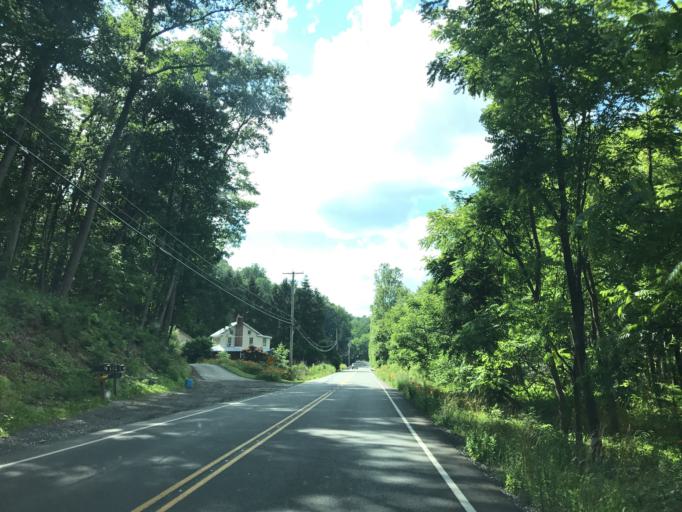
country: US
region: Pennsylvania
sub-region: York County
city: Glen Rock
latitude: 39.7702
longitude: -76.8279
